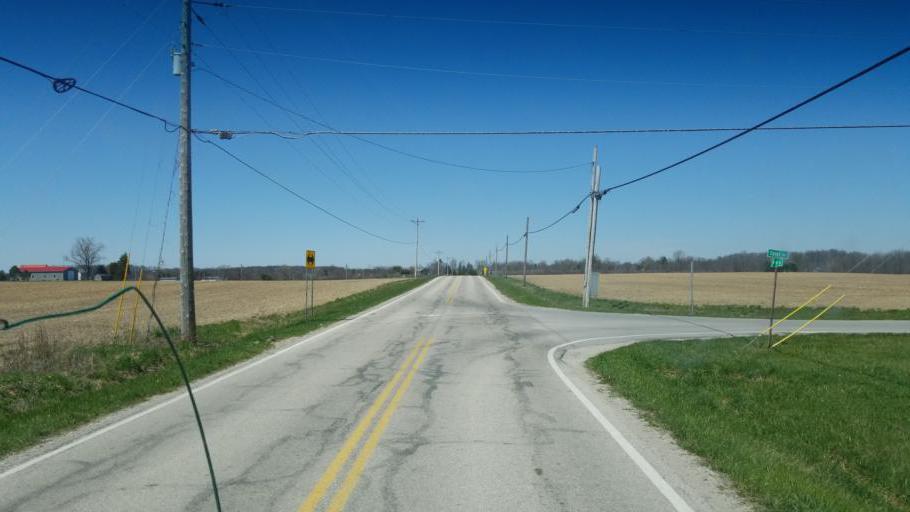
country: US
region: Ohio
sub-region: Huron County
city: Willard
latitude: 41.0793
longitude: -82.7387
